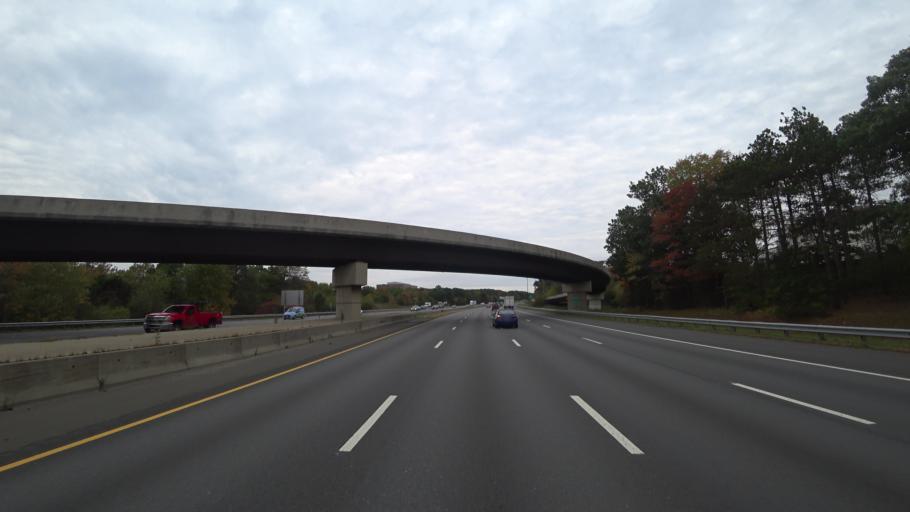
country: US
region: Massachusetts
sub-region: Middlesex County
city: Reading
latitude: 42.5207
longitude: -71.1335
